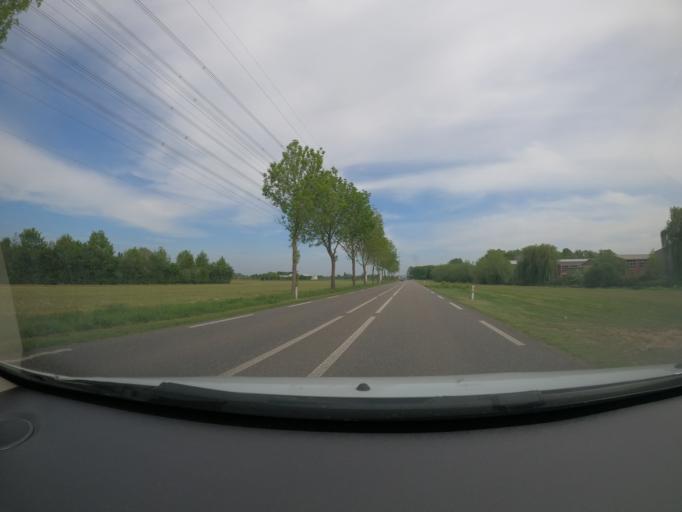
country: NL
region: Gelderland
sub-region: Oude IJsselstreek
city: Gendringen
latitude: 51.9041
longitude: 6.3720
